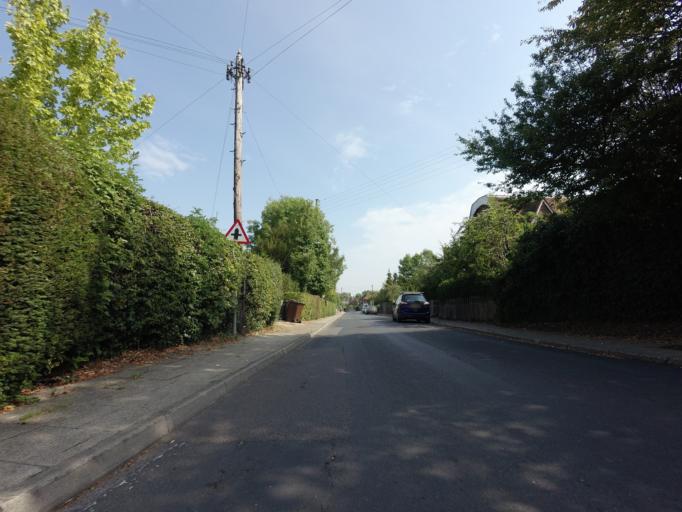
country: GB
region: England
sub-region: Kent
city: Headcorn
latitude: 51.1405
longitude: 0.5926
